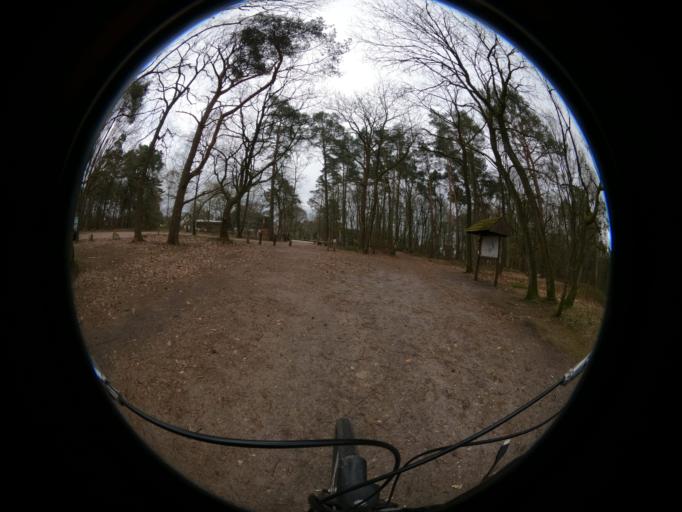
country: DE
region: Lower Saxony
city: Neu Wulmstorf
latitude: 53.4595
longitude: 9.8507
